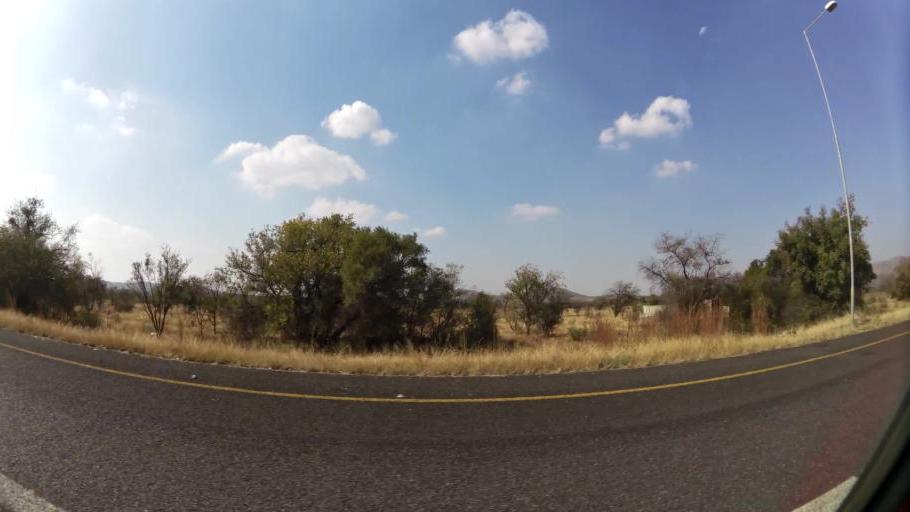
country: ZA
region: North-West
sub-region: Bojanala Platinum District Municipality
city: Rustenburg
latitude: -25.6174
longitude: 27.1548
